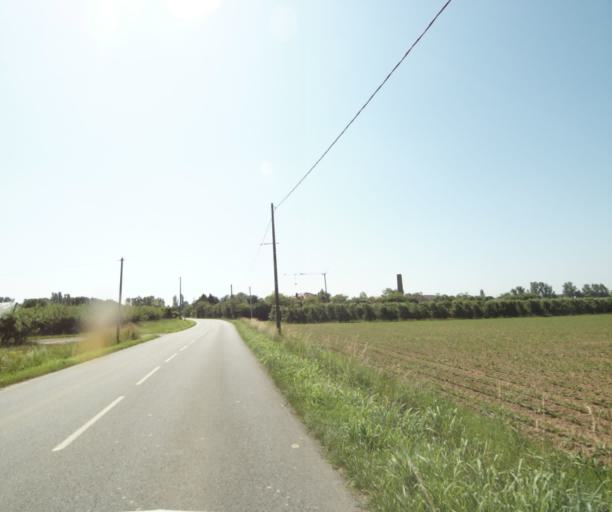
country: FR
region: Midi-Pyrenees
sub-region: Departement du Tarn-et-Garonne
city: Montbeton
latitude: 44.0293
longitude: 1.3106
